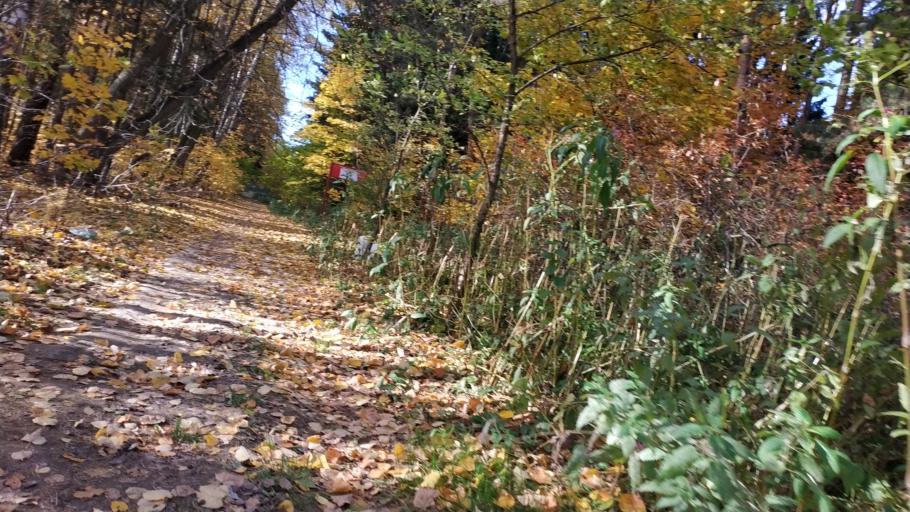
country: RU
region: Moskovskaya
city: Sheremet'yevskiy
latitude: 55.9872
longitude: 37.4845
